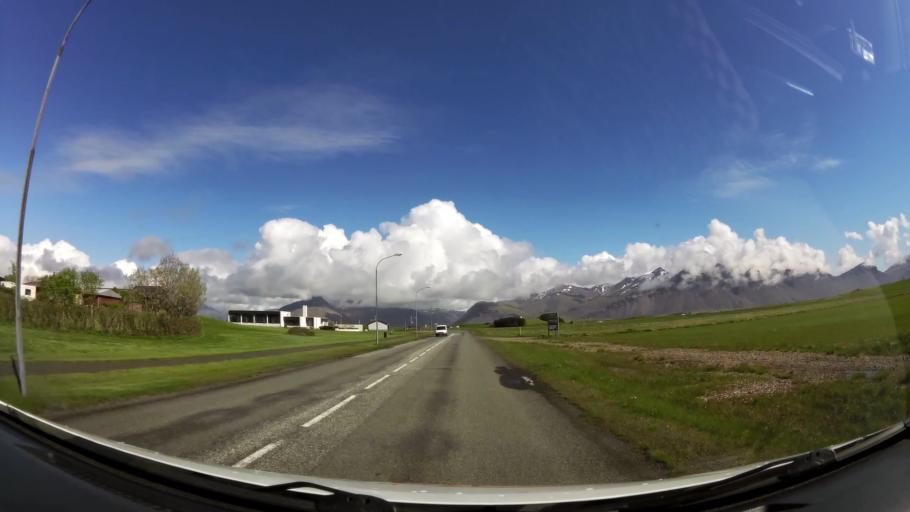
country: IS
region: East
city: Hoefn
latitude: 64.2621
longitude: -15.2027
